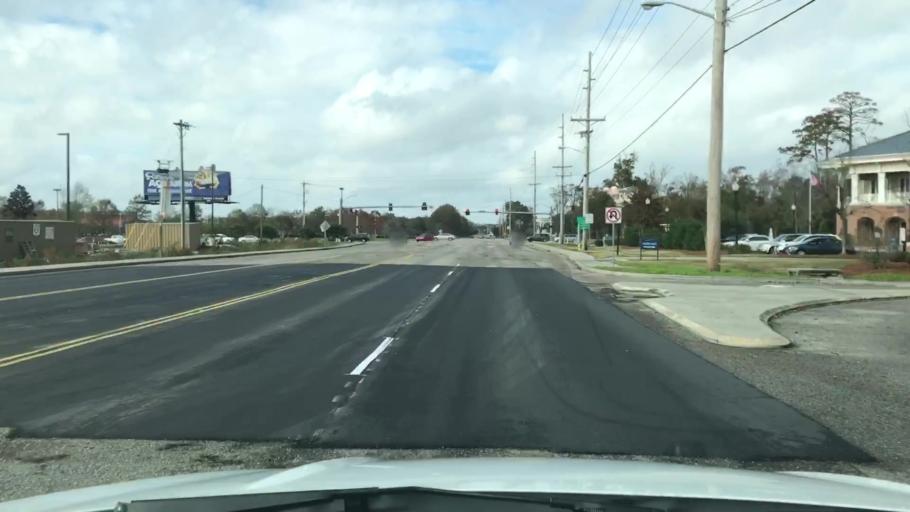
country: US
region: South Carolina
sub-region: Horry County
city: Myrtle Beach
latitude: 33.7148
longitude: -78.8717
